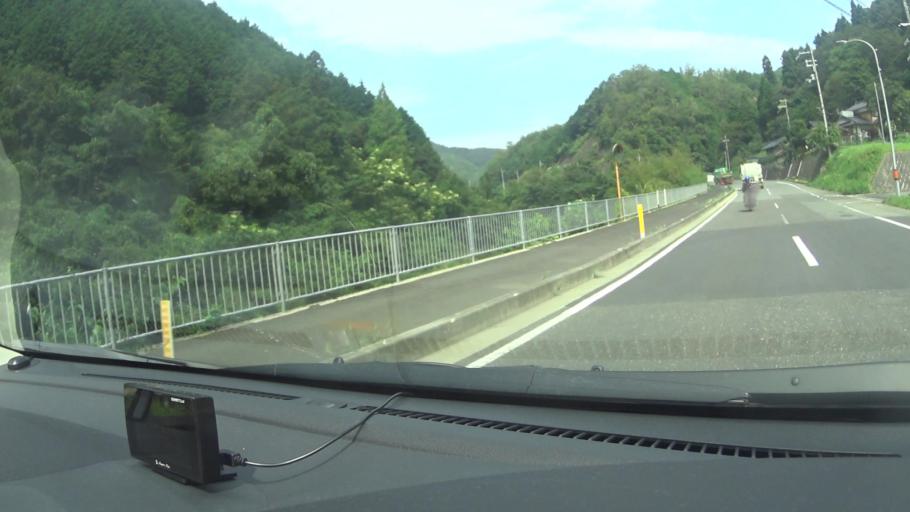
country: JP
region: Kyoto
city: Ayabe
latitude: 35.2578
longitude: 135.2764
